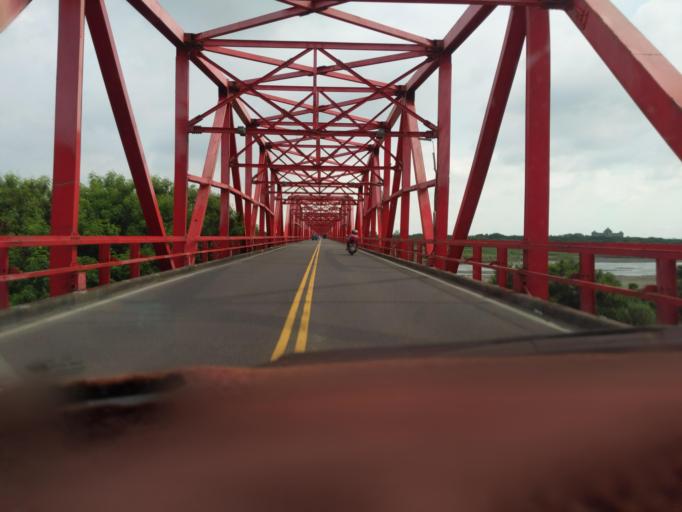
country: TW
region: Taiwan
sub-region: Yunlin
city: Douliu
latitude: 23.8164
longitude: 120.4617
